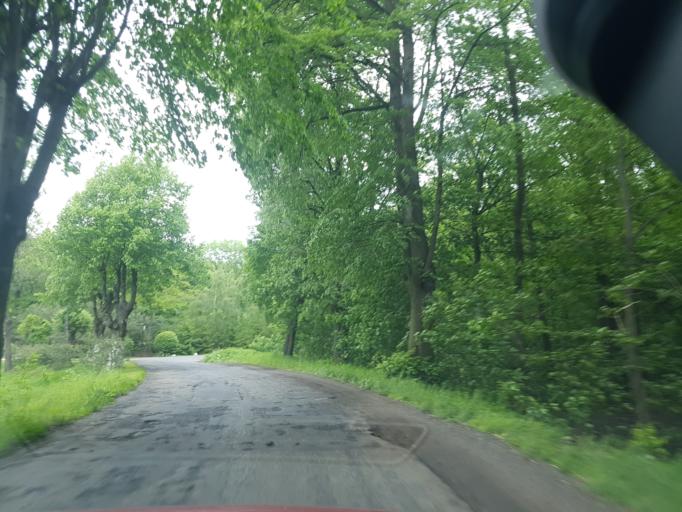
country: PL
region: Lower Silesian Voivodeship
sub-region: Powiat wroclawski
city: Katy Wroclawskie
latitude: 50.9805
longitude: 16.7573
